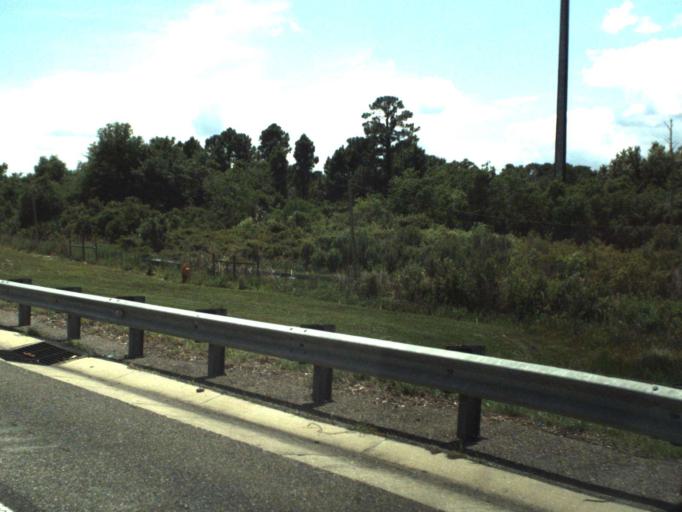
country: US
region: Florida
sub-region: Volusia County
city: Deltona
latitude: 28.8920
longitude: -81.2780
